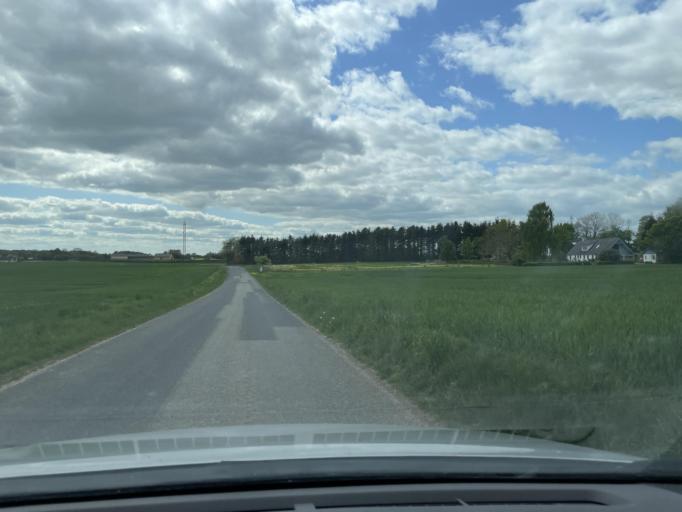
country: DK
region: Central Jutland
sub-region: Skanderborg Kommune
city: Skanderborg
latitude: 55.9242
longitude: 9.9783
